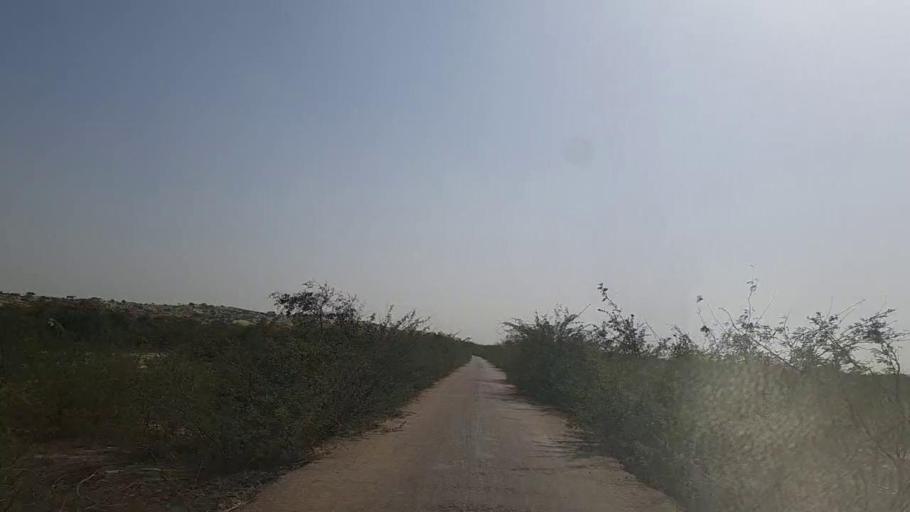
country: PK
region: Sindh
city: Naukot
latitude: 24.5742
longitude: 69.2935
